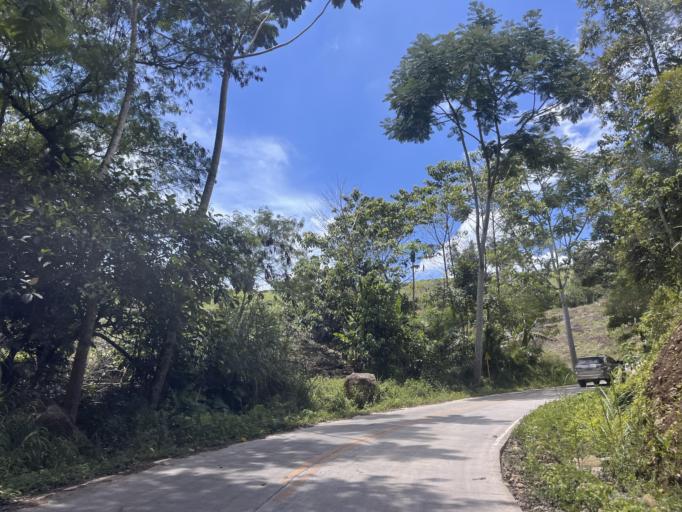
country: PH
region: Northern Mindanao
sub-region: Province of Bukidnon
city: Kisolon
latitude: 8.3096
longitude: 124.9645
